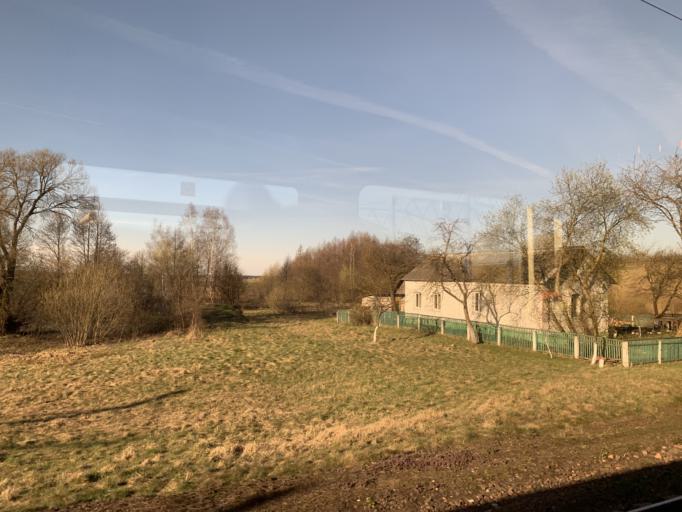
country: BY
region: Minsk
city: Nasilava
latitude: 54.3149
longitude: 26.7958
